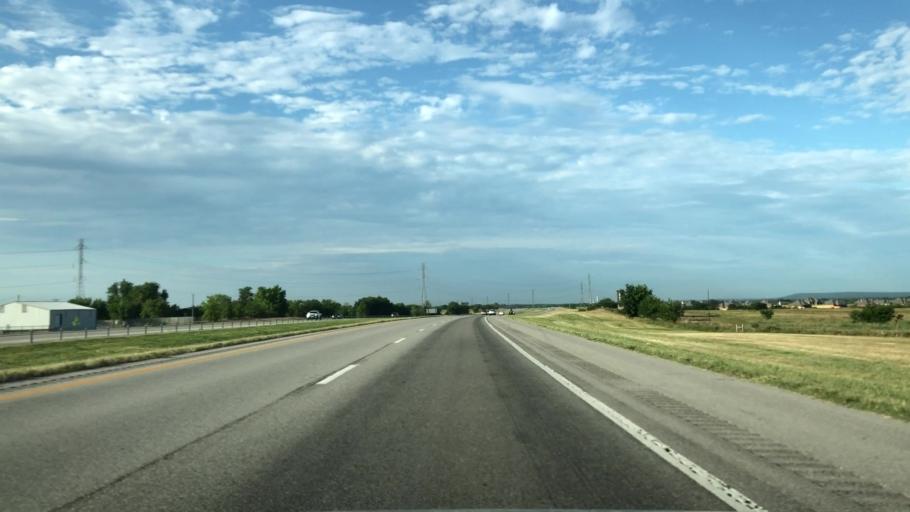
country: US
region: Oklahoma
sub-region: Osage County
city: Skiatook
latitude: 36.3516
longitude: -95.9210
